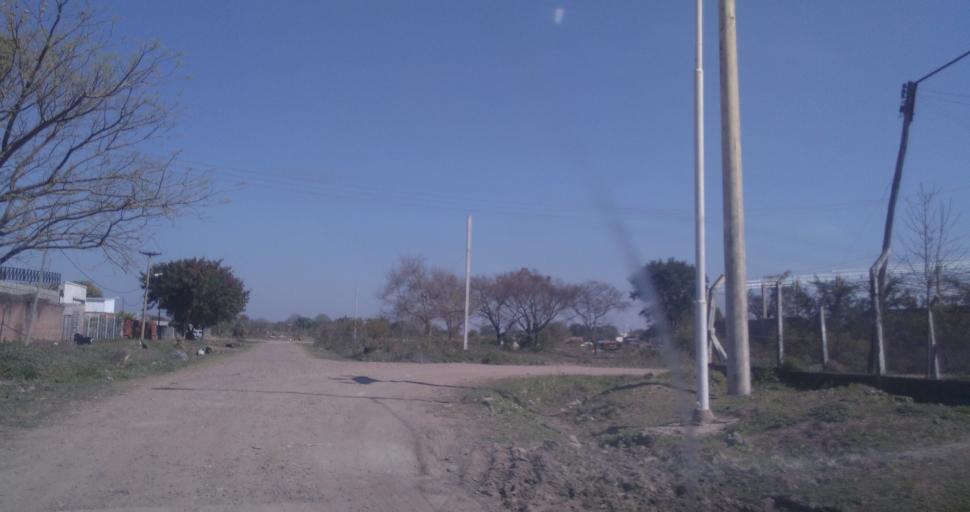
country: AR
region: Chaco
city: Fontana
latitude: -27.4328
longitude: -59.0291
